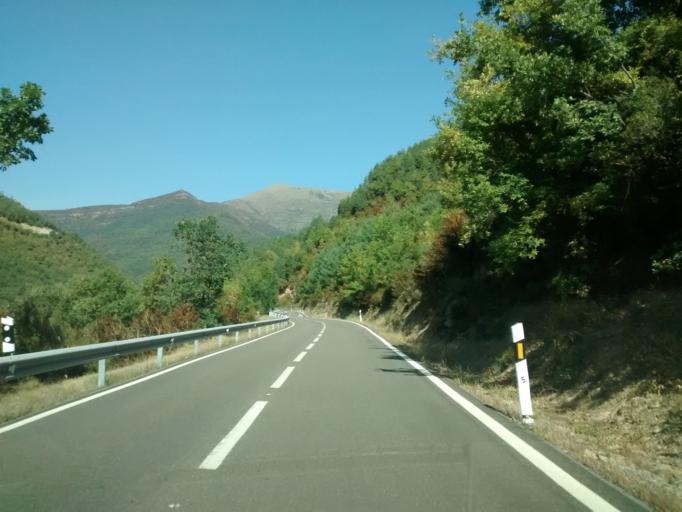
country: ES
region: Aragon
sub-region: Provincia de Huesca
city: Fiscal
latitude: 42.5212
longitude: -0.1309
